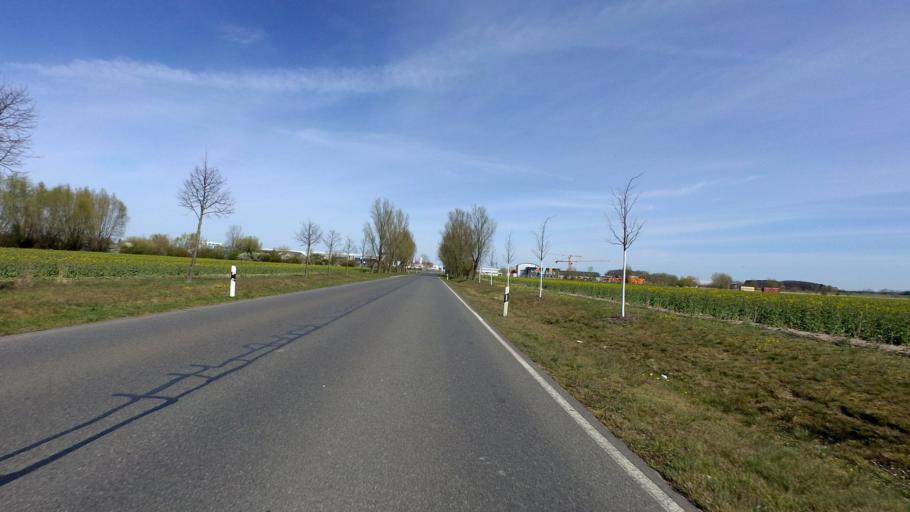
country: DE
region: Brandenburg
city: Rangsdorf
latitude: 52.3173
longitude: 13.4696
